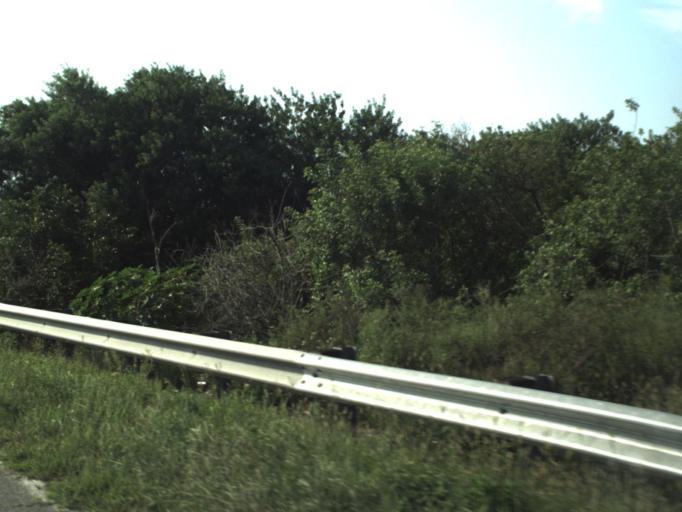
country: US
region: Florida
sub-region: Hendry County
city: Clewiston
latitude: 26.7273
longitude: -80.8529
